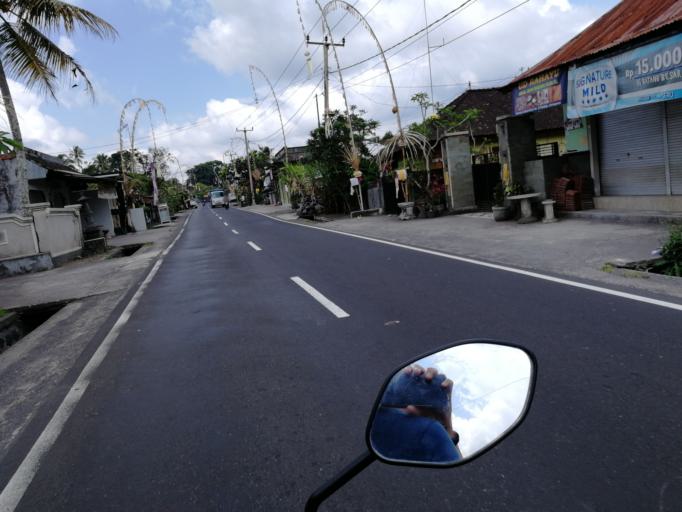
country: ID
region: Bali
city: Banjar Wangsian
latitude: -8.4284
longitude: 115.4331
